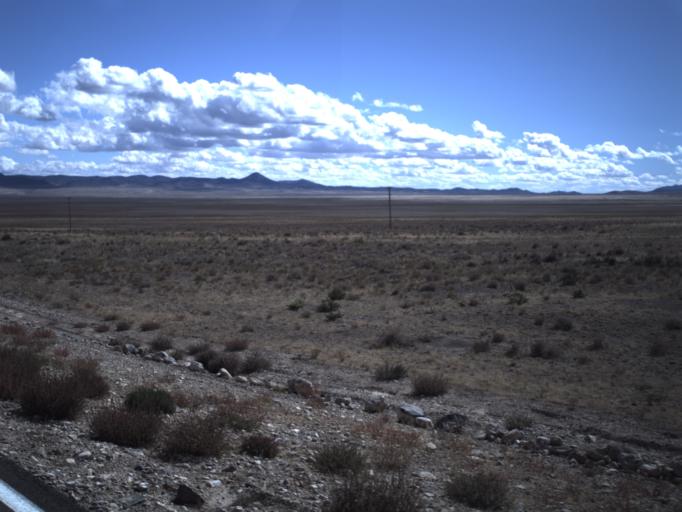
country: US
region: Utah
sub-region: Beaver County
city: Milford
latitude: 38.4864
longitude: -113.4561
